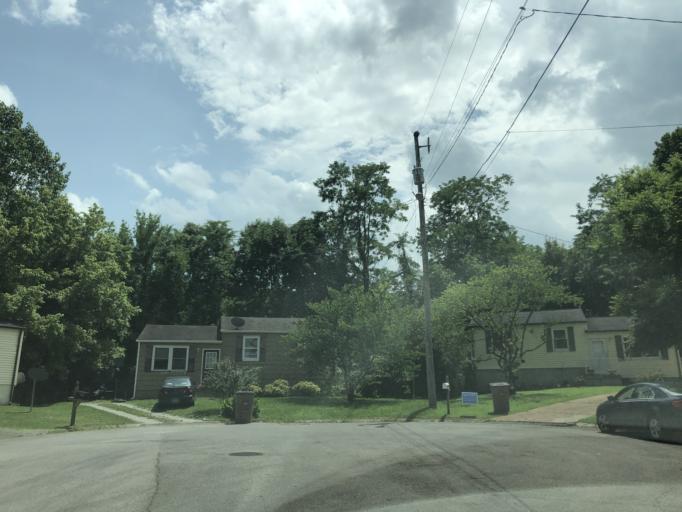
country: US
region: Tennessee
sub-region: Williamson County
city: Brentwood Estates
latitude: 36.0619
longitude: -86.6924
